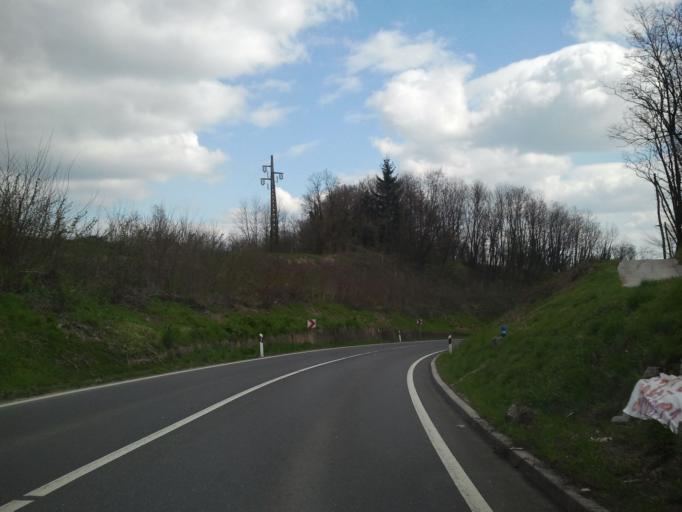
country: HR
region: Zagrebacka
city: Kerestinec
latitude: 45.7364
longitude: 15.7906
